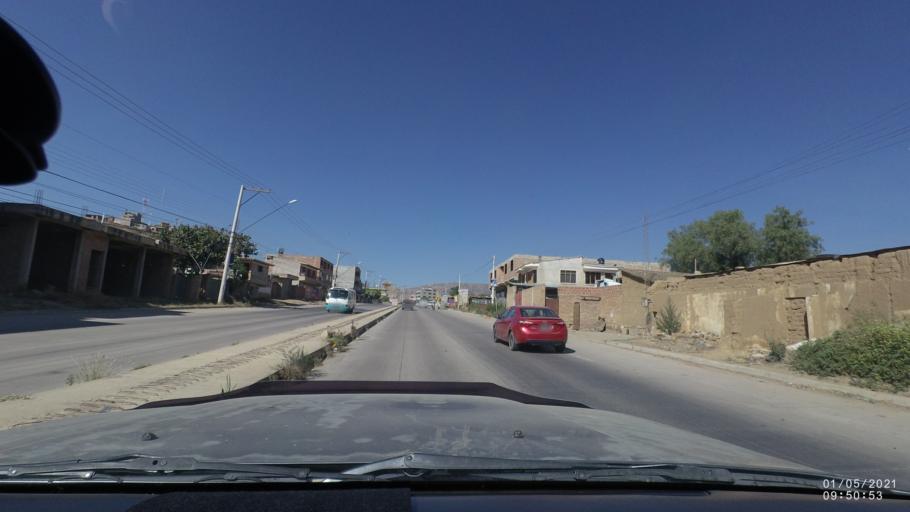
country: BO
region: Cochabamba
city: Cochabamba
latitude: -17.4680
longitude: -66.1704
